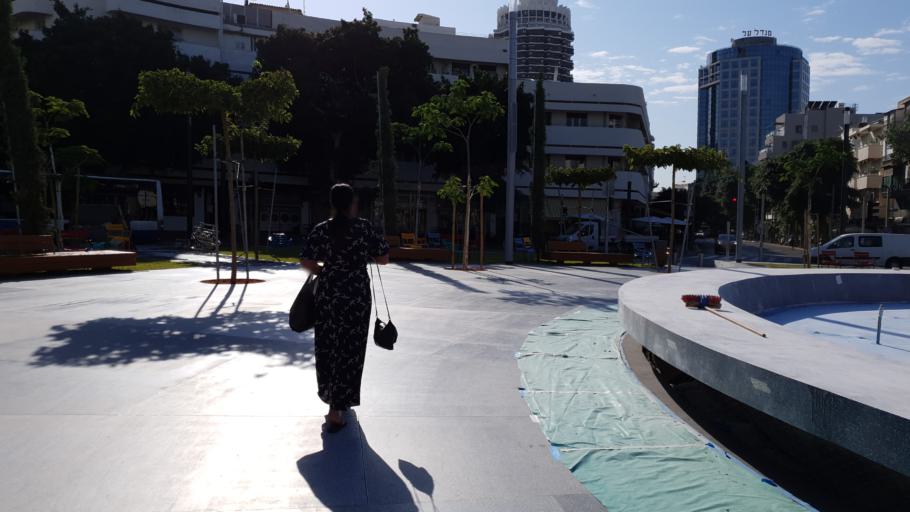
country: IL
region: Tel Aviv
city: Tel Aviv
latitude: 32.0781
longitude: 34.7743
